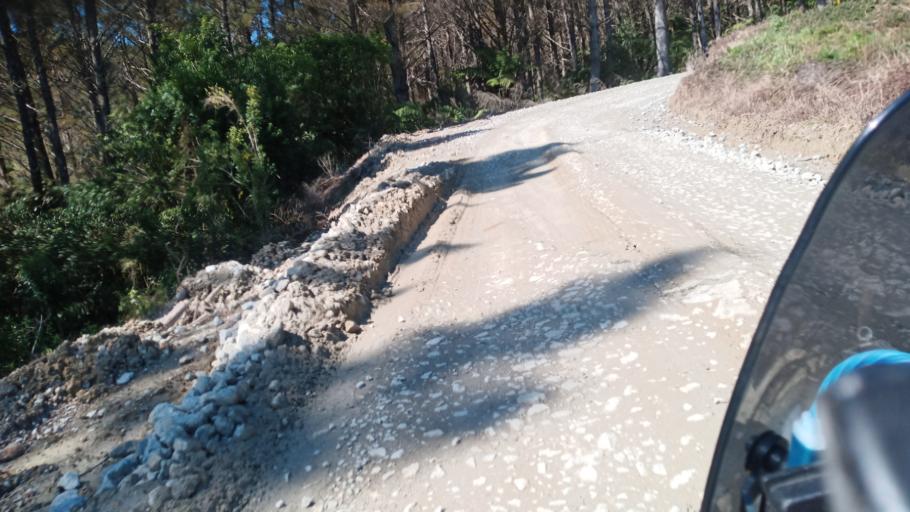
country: NZ
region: Gisborne
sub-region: Gisborne District
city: Gisborne
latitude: -38.8960
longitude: 177.8045
